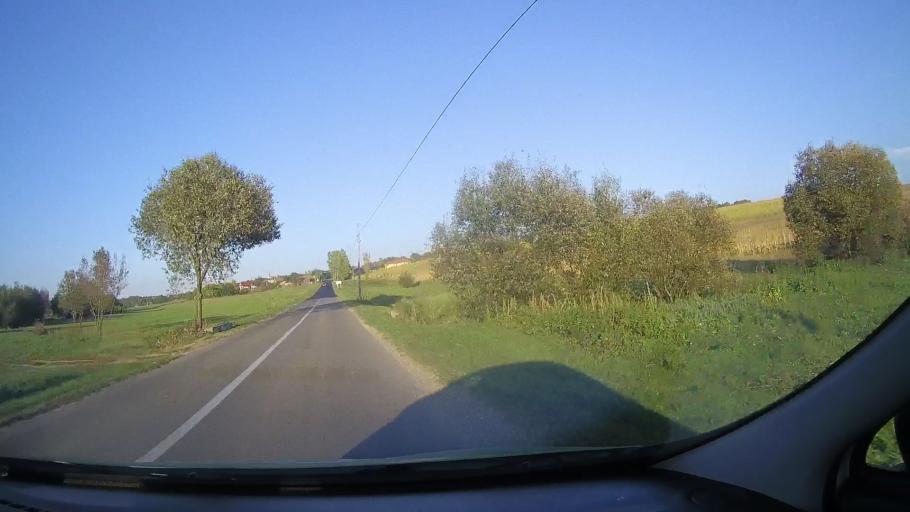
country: RO
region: Bihor
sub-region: Comuna Paleu
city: Paleu
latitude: 47.1322
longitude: 21.9852
